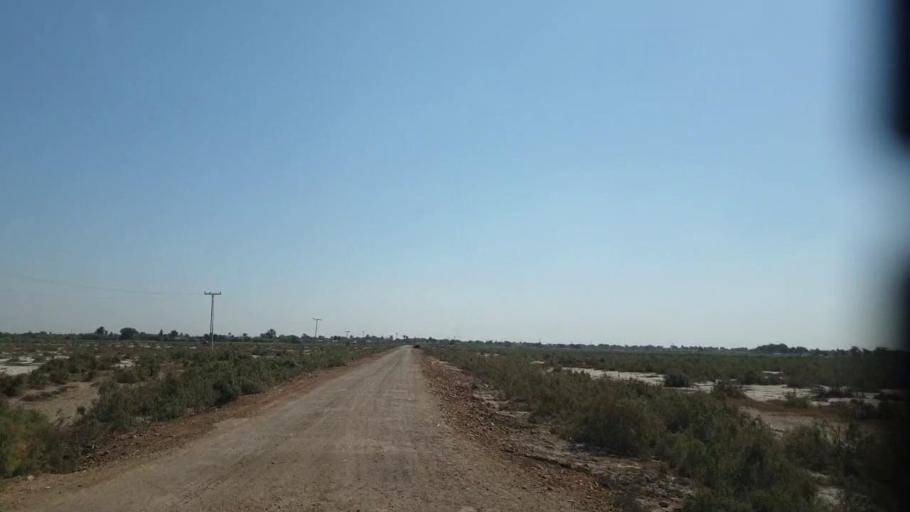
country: PK
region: Sindh
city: Mirpur Khas
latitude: 25.5870
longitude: 69.1081
